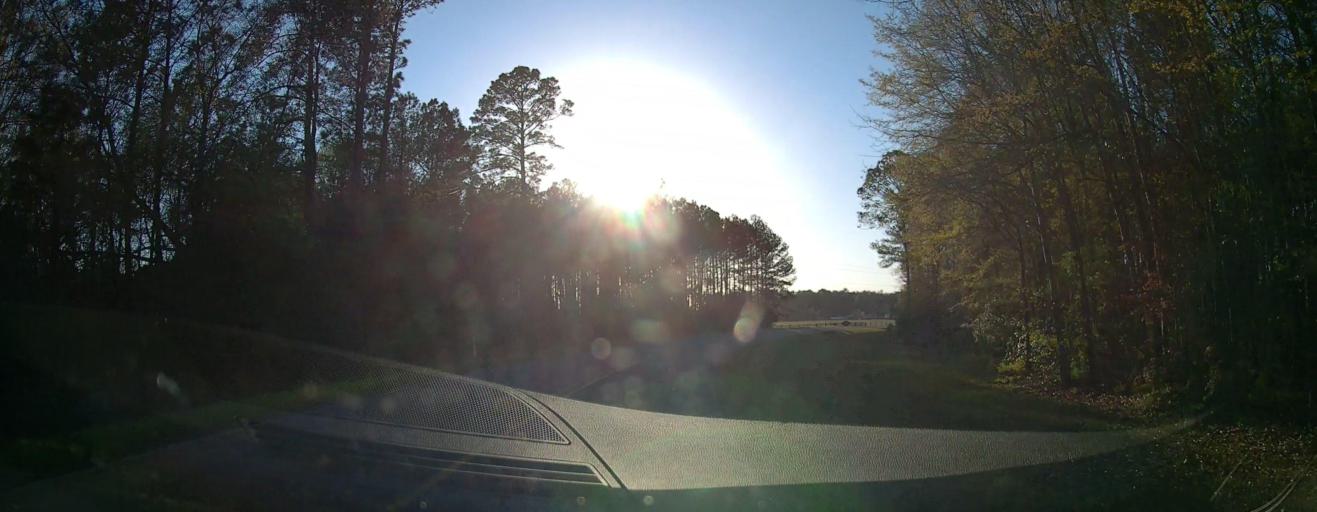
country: US
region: Georgia
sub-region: Wilkinson County
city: Gordon
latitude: 32.8830
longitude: -83.2899
